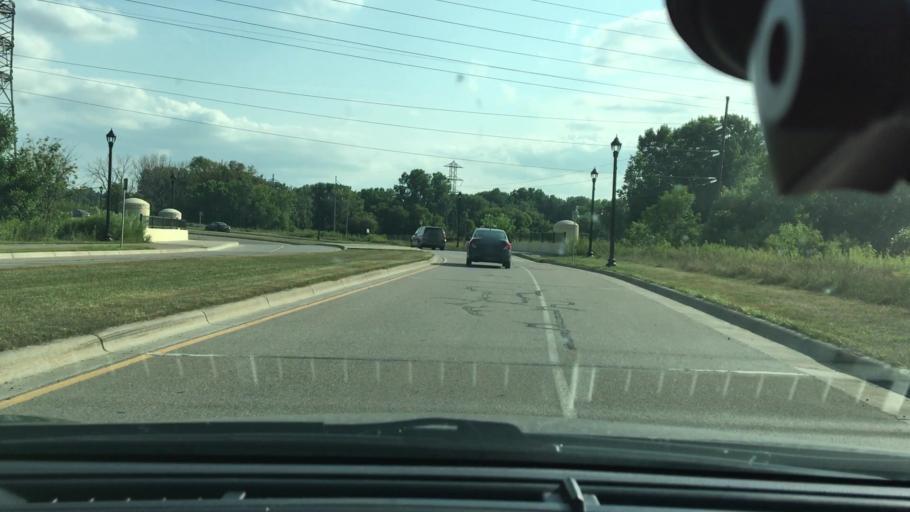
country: US
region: Minnesota
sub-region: Hennepin County
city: Minneapolis
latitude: 44.9779
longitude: -93.2957
